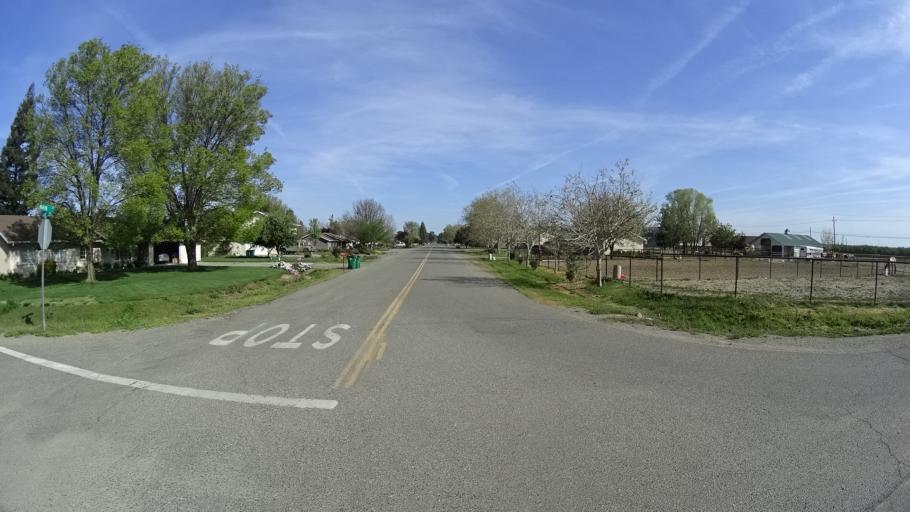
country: US
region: California
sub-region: Glenn County
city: Willows
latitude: 39.6112
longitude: -122.1952
